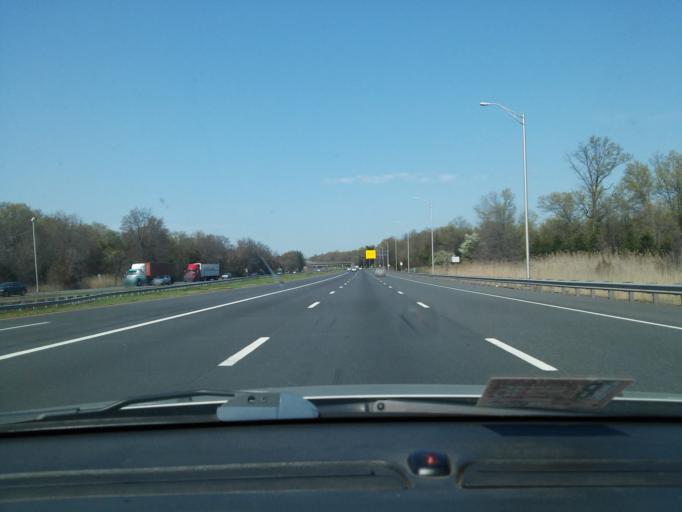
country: US
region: New Jersey
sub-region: Somerset County
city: Bedminster
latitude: 40.6440
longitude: -74.6601
